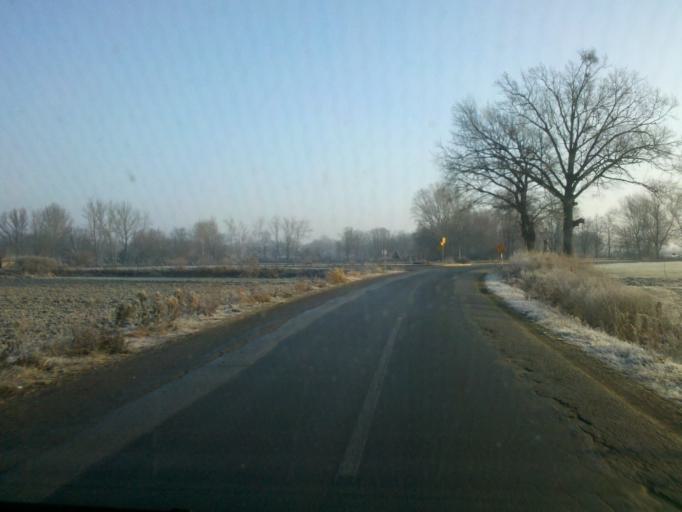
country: HR
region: Varazdinska
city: Ludbreg
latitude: 46.2766
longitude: 16.7088
